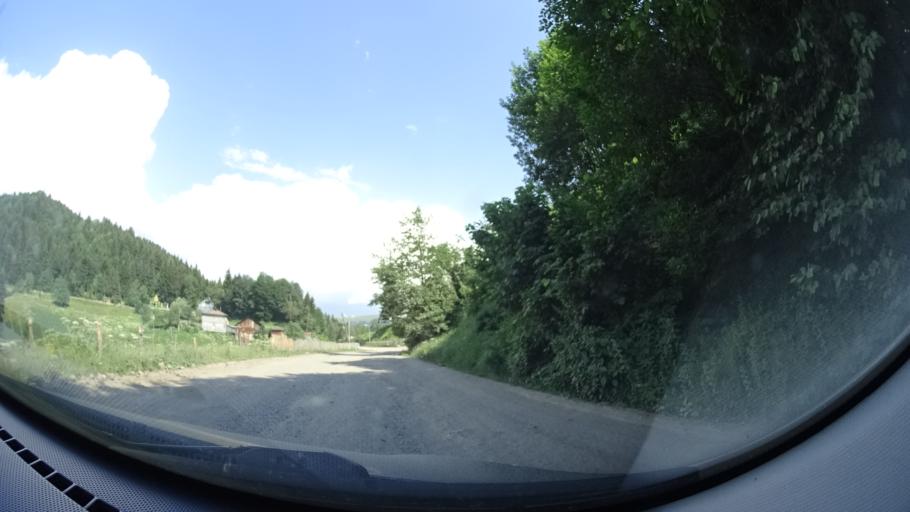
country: GE
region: Ajaria
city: Dioknisi
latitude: 41.6499
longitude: 42.4674
